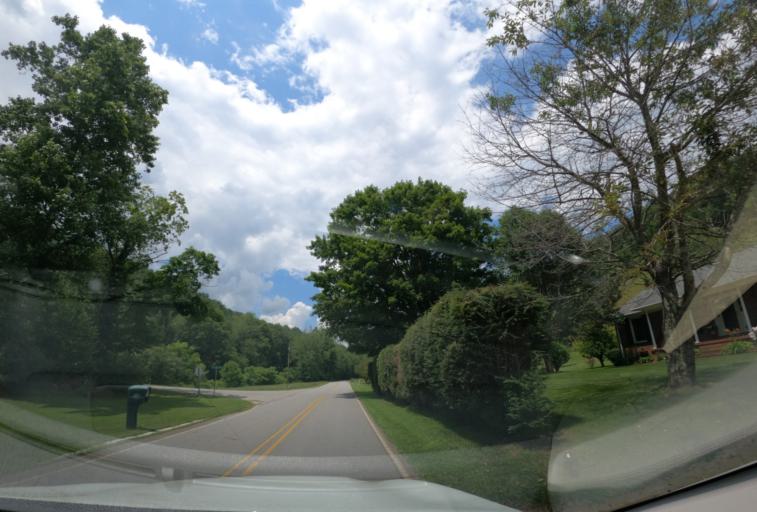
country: US
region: North Carolina
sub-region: Haywood County
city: Waynesville
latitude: 35.4127
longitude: -82.9058
